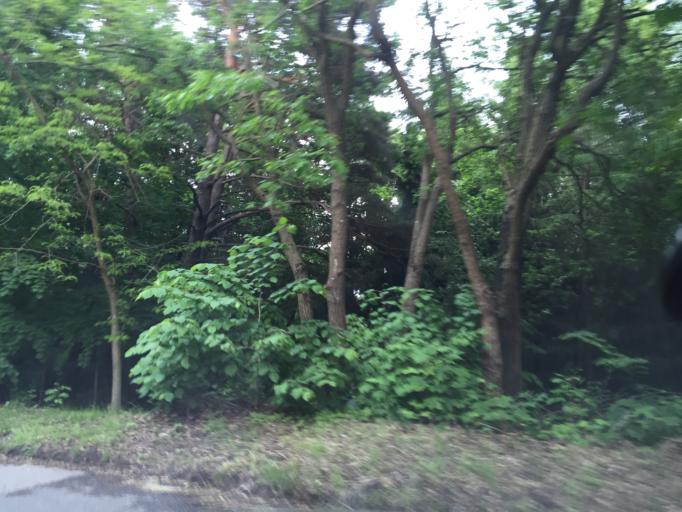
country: LT
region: Klaipedos apskritis
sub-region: Klaipeda
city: Klaipeda
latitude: 55.7667
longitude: 21.0907
